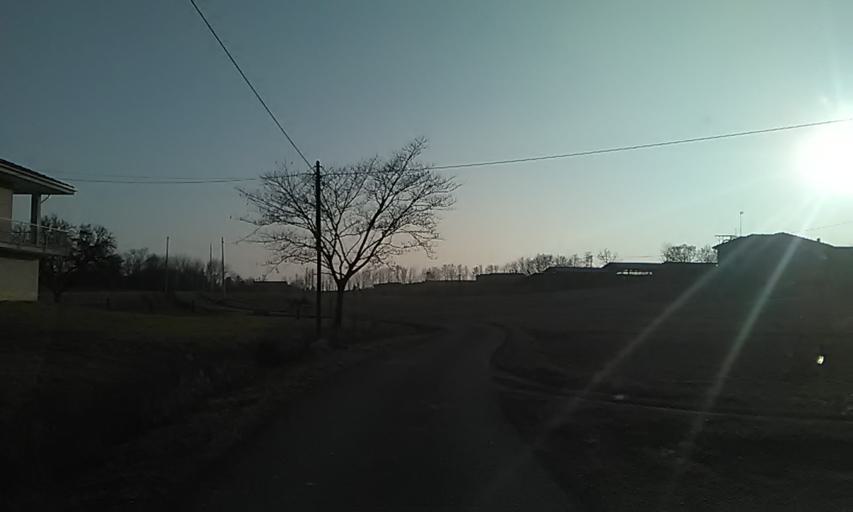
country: IT
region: Piedmont
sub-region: Provincia di Biella
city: Dorzano
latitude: 45.4109
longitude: 8.1175
